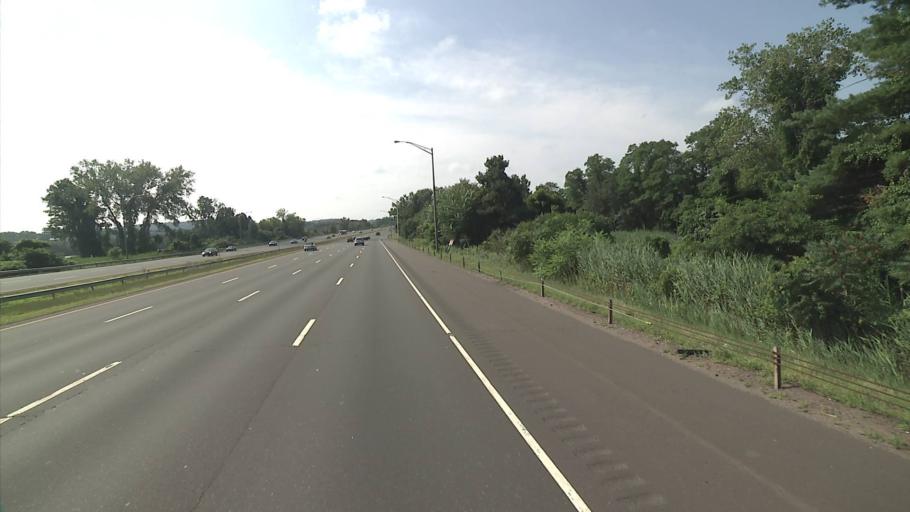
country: US
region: Connecticut
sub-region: New Haven County
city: North Haven
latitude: 41.3630
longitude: -72.8689
